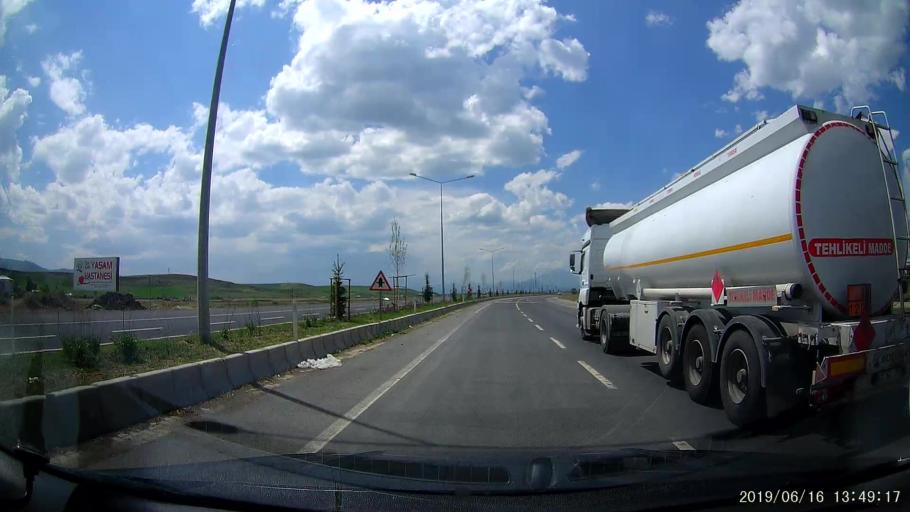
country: TR
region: Agri
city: Agri
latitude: 39.7160
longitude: 42.9933
